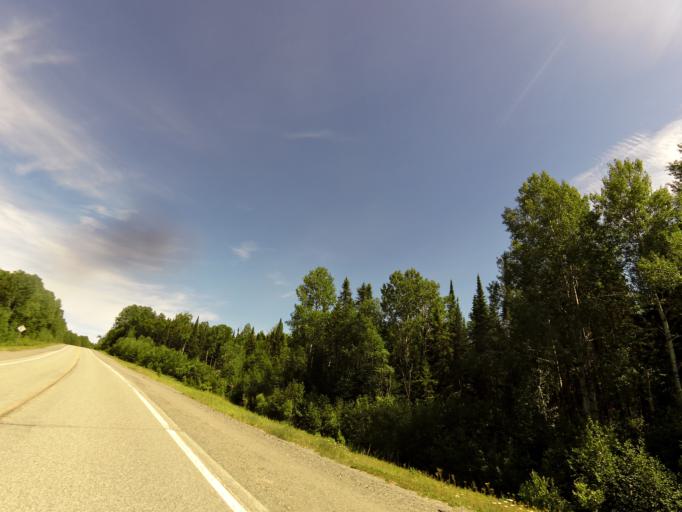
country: CA
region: Quebec
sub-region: Nord-du-Quebec
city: Lebel-sur-Quevillon
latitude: 48.8603
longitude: -77.1351
